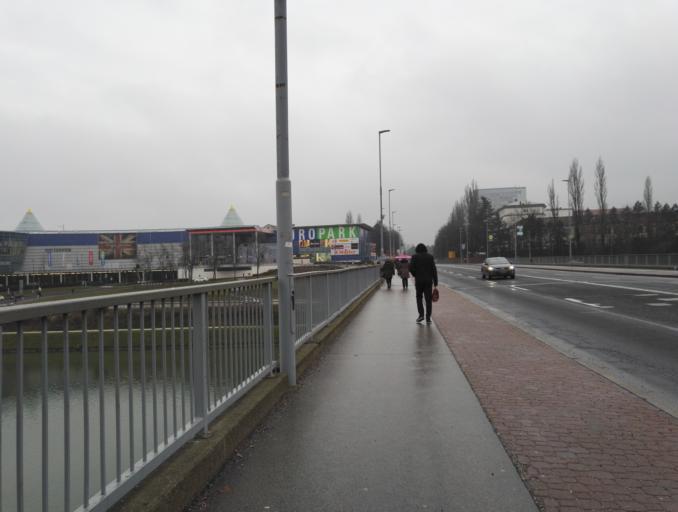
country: SI
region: Maribor
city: Maribor
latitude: 46.5561
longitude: 15.6508
